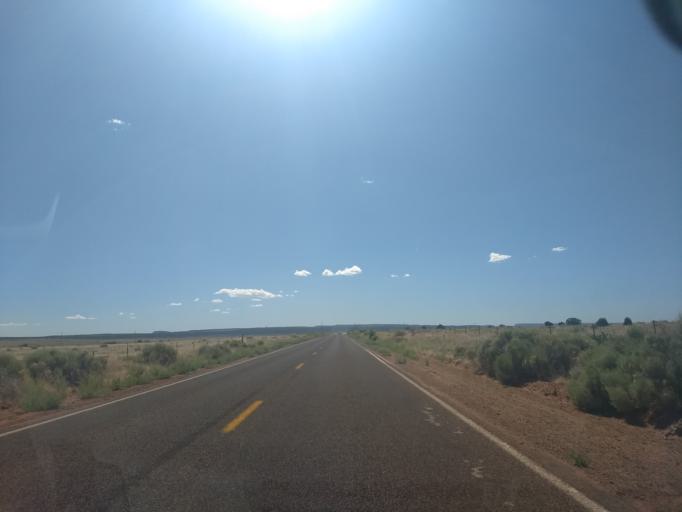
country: US
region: Arizona
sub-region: Mohave County
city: Colorado City
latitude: 36.9469
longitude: -112.9490
